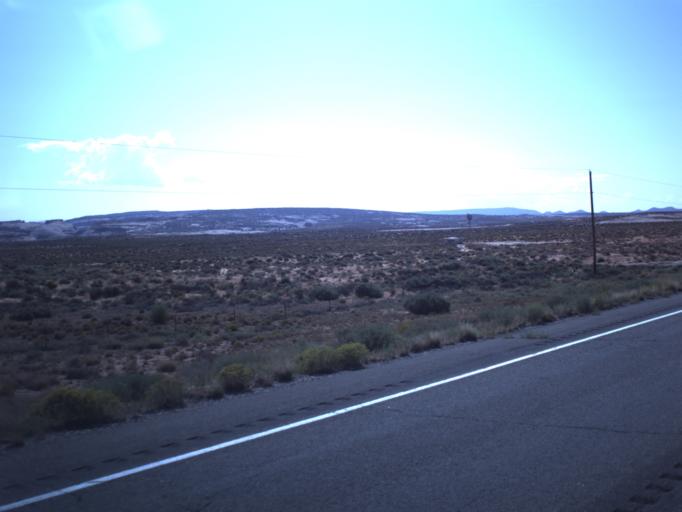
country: US
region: Utah
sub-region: San Juan County
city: Blanding
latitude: 37.0843
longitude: -109.5480
